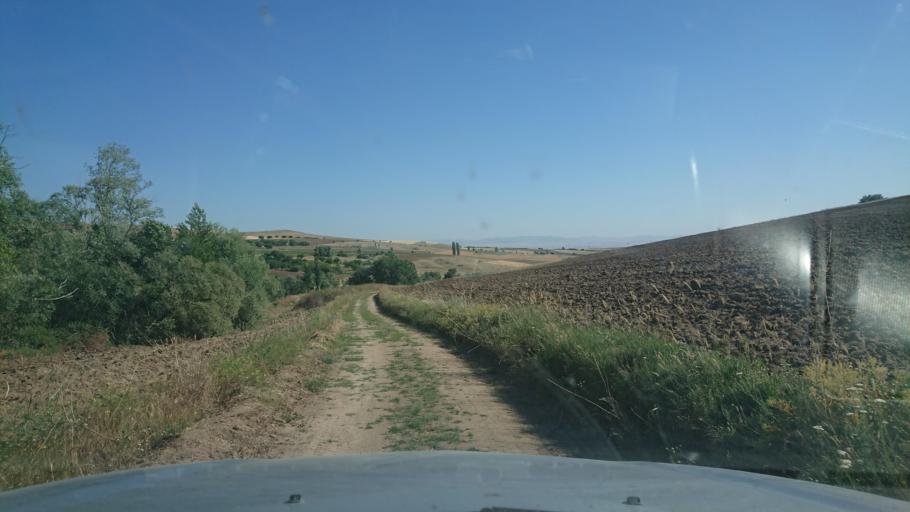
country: TR
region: Aksaray
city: Agacoren
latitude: 38.8406
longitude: 33.9257
